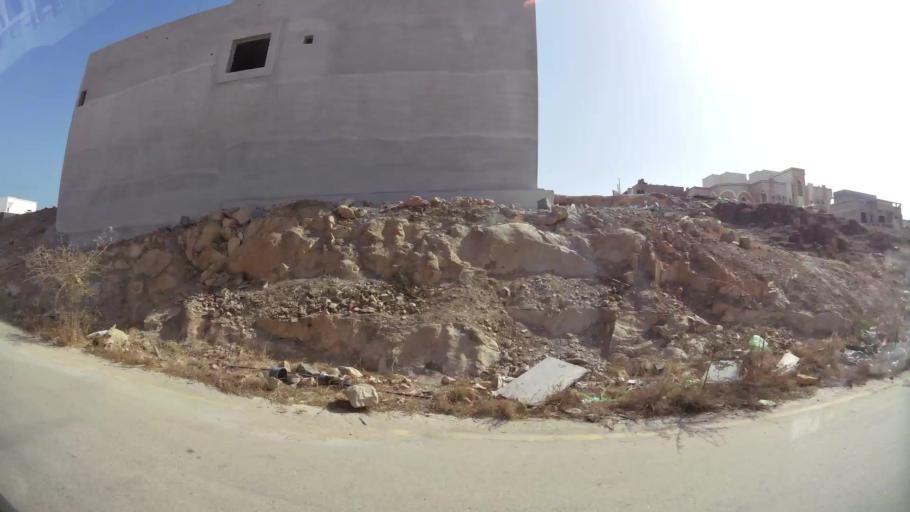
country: OM
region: Zufar
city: Salalah
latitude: 16.9997
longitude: 54.0164
